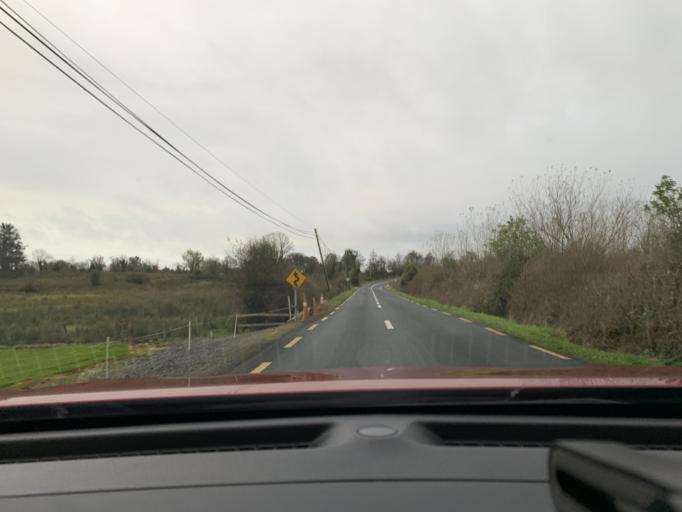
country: IE
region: Connaught
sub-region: Sligo
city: Ballymote
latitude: 53.9930
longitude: -8.5244
